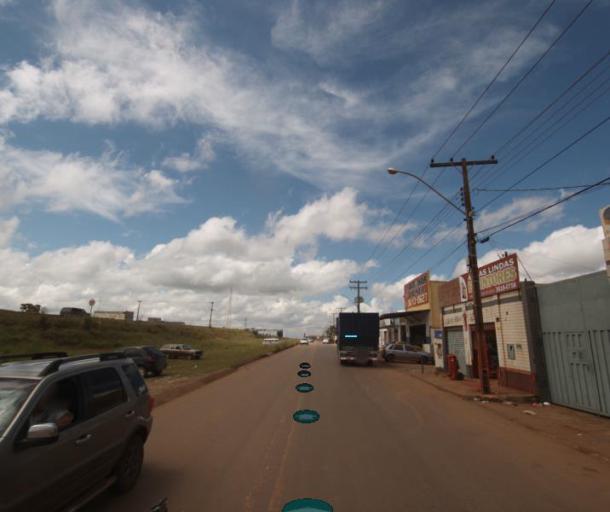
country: BR
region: Federal District
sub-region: Brasilia
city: Brasilia
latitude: -15.7487
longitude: -48.2640
